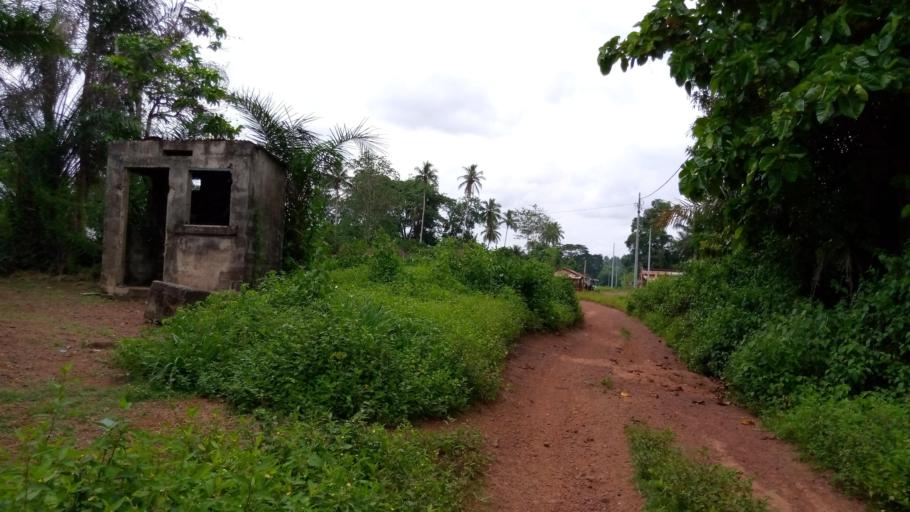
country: SL
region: Southern Province
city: Rotifunk
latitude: 8.1895
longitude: -12.5665
